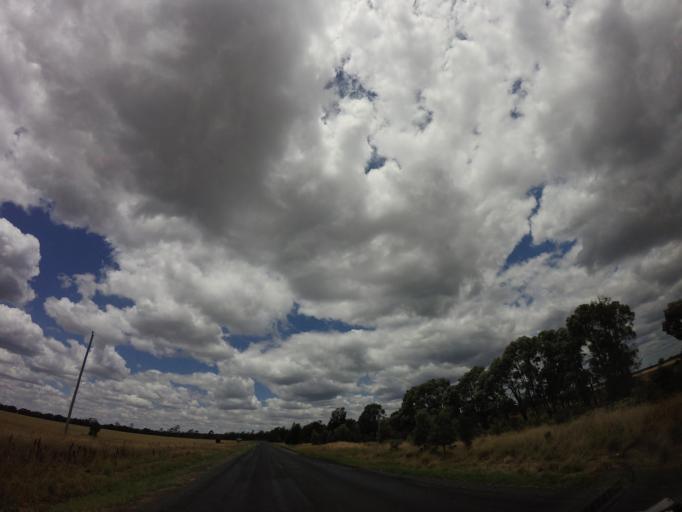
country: AU
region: Queensland
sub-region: Goondiwindi
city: Goondiwindi
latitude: -28.0057
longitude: 150.9144
